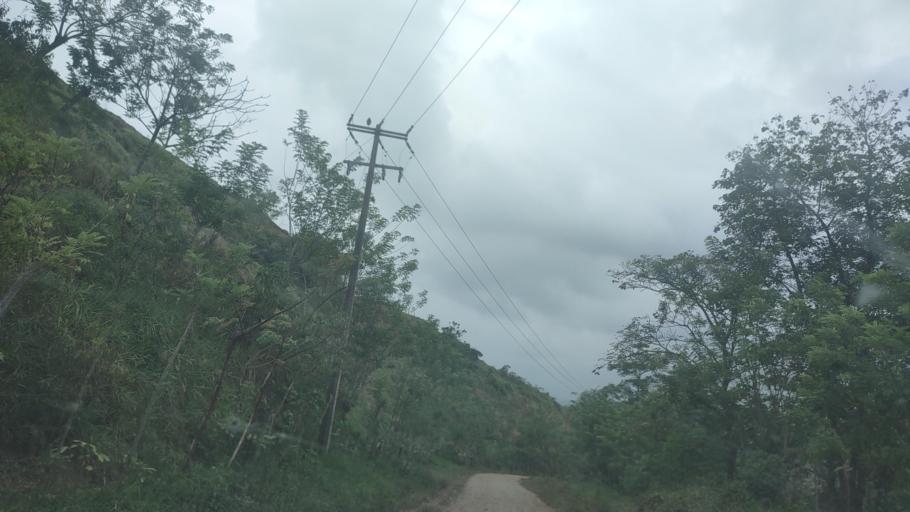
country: MX
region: Tabasco
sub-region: Huimanguillo
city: Francisco Rueda
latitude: 17.4393
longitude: -94.0260
